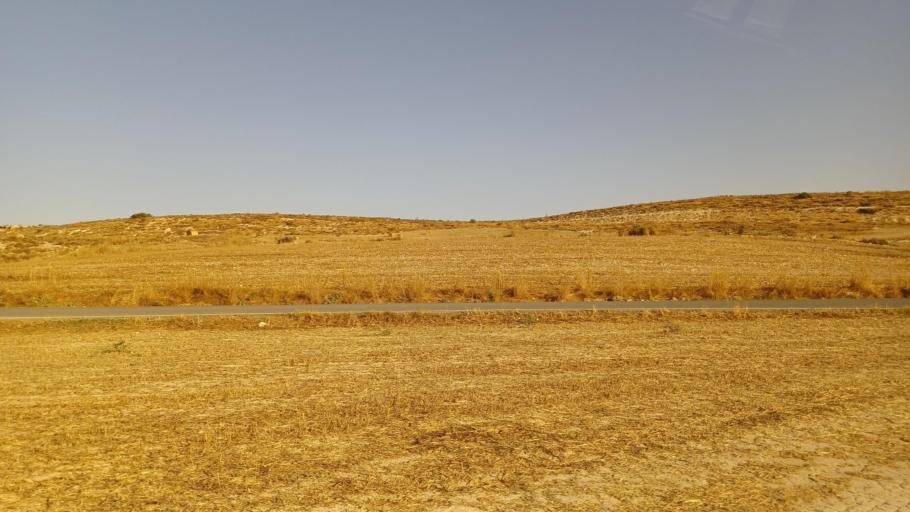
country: CY
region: Larnaka
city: Athienou
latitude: 35.0425
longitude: 33.5156
